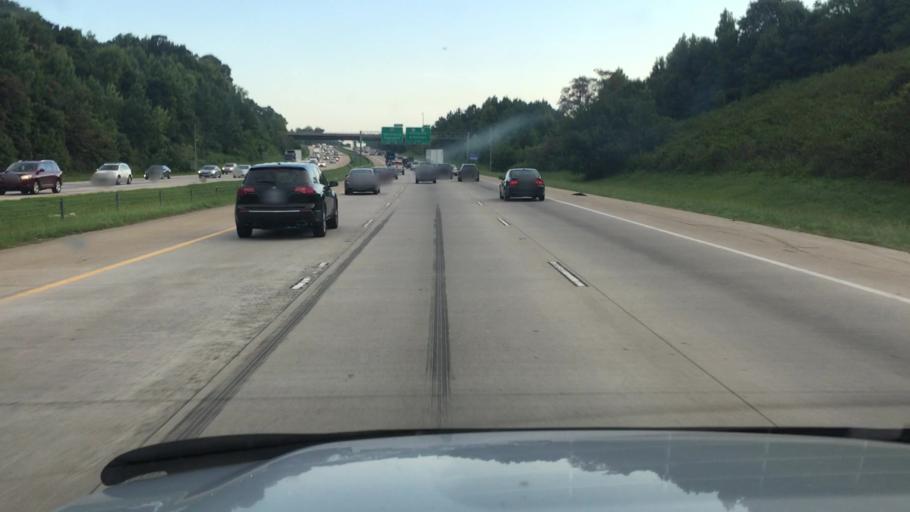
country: US
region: North Carolina
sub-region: Gaston County
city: Belmont
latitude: 35.2157
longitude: -80.9688
